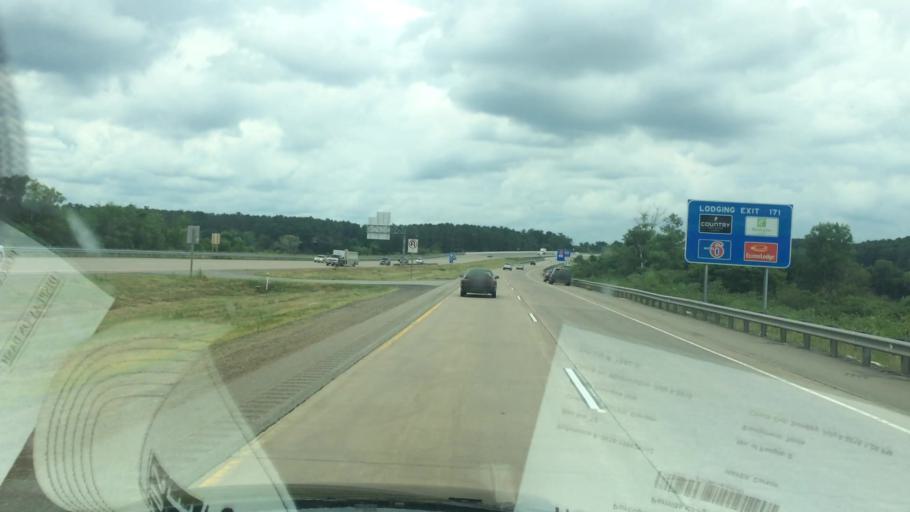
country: US
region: Wisconsin
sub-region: Marathon County
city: Rothschild
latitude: 44.8975
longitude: -89.6256
